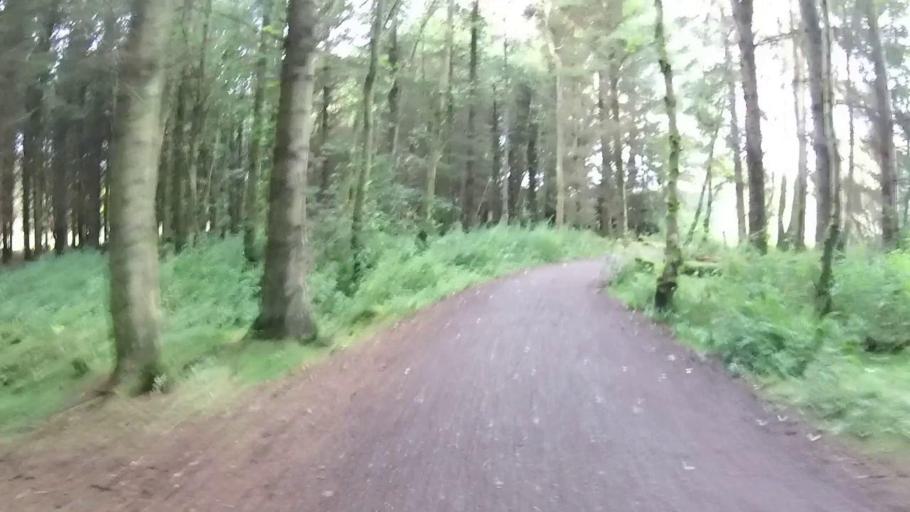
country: GB
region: Scotland
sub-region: Perth and Kinross
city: Kinross
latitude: 56.2130
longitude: -3.4042
